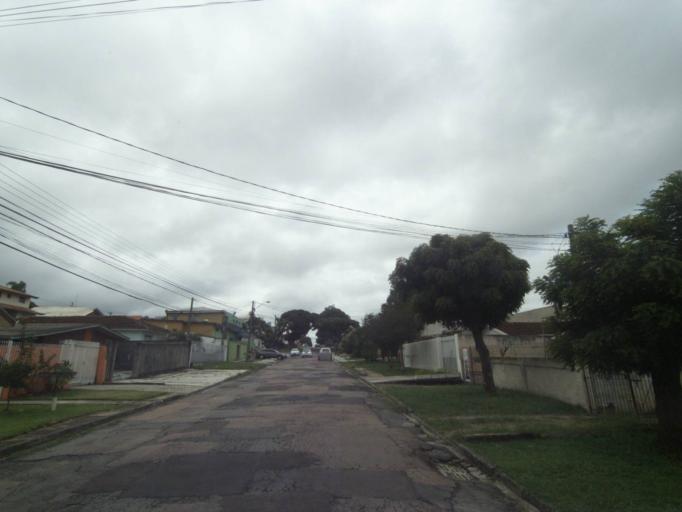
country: BR
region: Parana
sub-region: Curitiba
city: Curitiba
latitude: -25.4882
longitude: -49.3006
